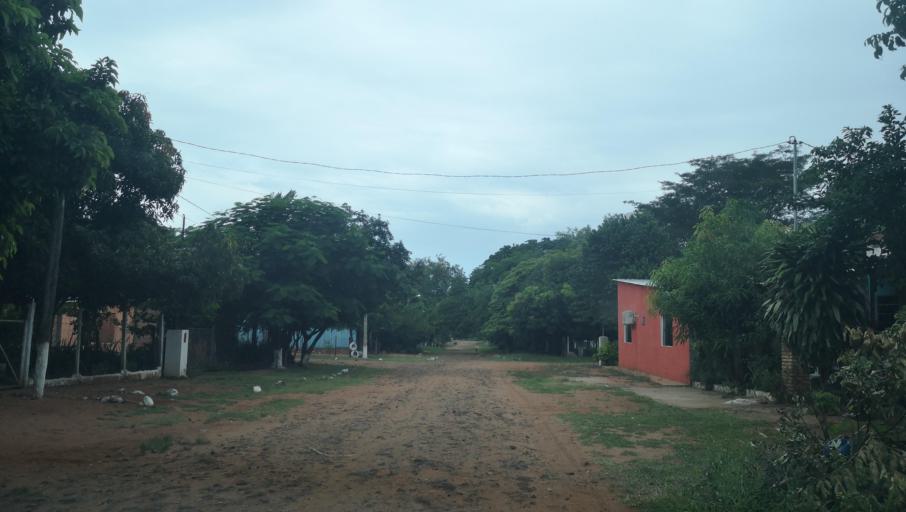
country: PY
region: San Pedro
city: Capiibary
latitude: -24.7256
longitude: -56.0127
